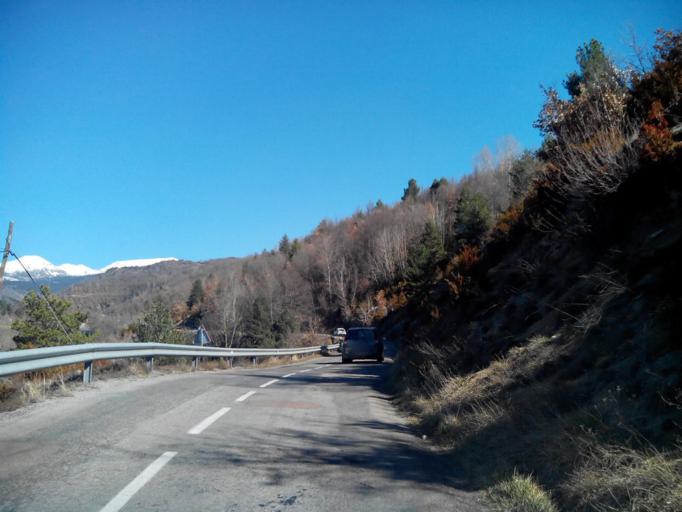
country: ES
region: Catalonia
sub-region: Provincia de Lleida
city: Lles de Cerdanya
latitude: 42.3631
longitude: 1.6853
